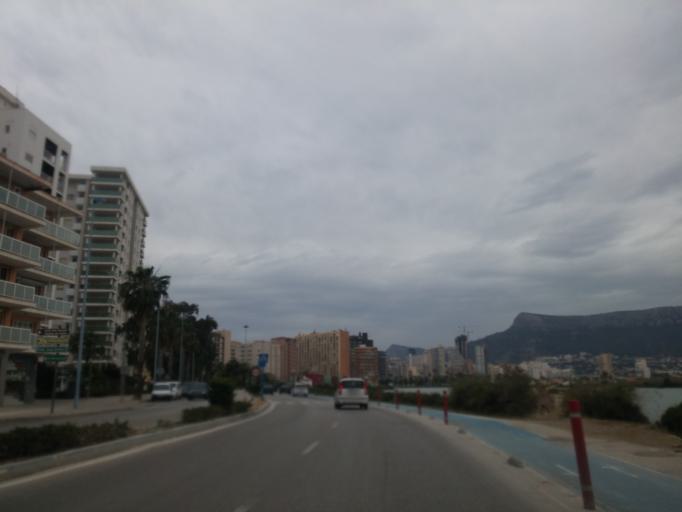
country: ES
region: Valencia
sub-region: Provincia de Alicante
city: Calp
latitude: 38.6429
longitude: 0.0688
